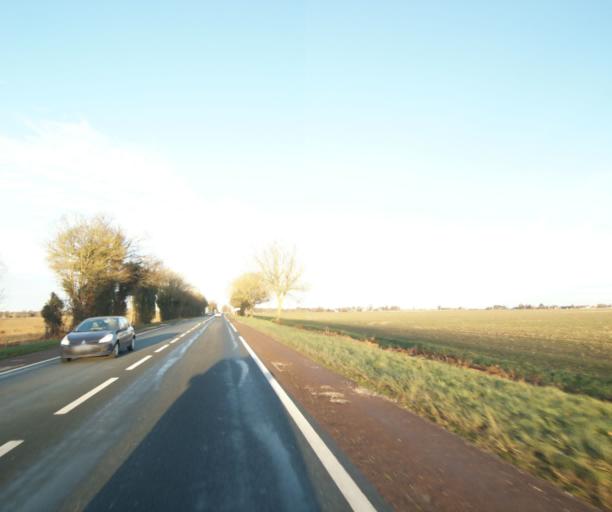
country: FR
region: Poitou-Charentes
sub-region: Departement de la Charente-Maritime
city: Nieul-les-Saintes
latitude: 45.7981
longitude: -0.7399
